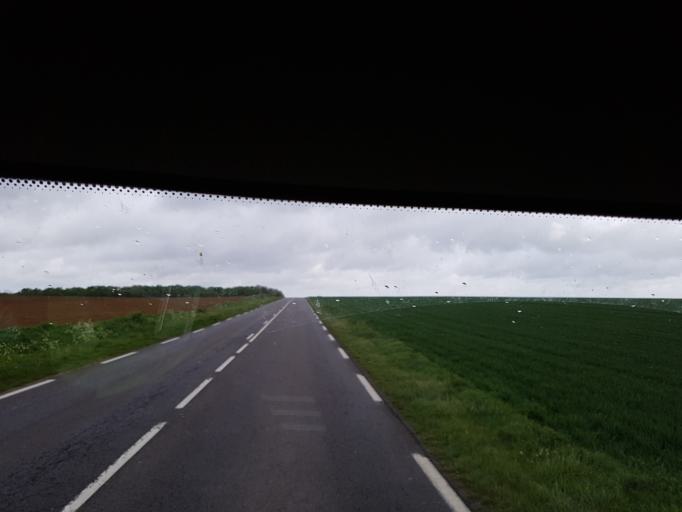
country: FR
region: Picardie
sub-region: Departement de l'Aisne
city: Crouy
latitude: 49.4334
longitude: 3.3535
